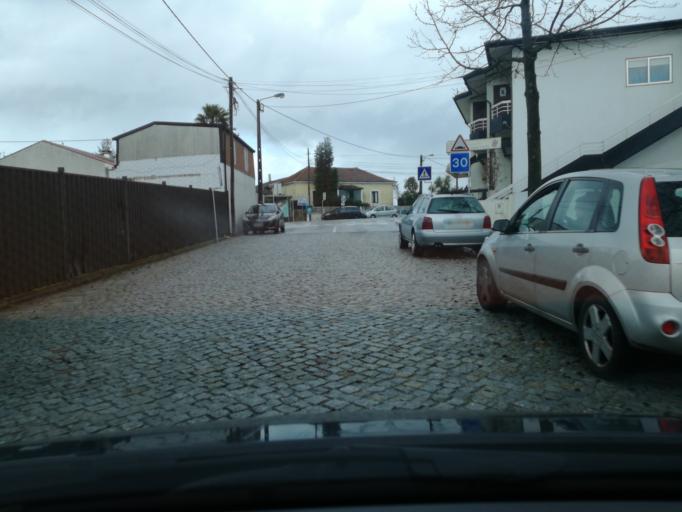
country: PT
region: Porto
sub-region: Valongo
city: Alfena
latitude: 41.2504
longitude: -8.5483
